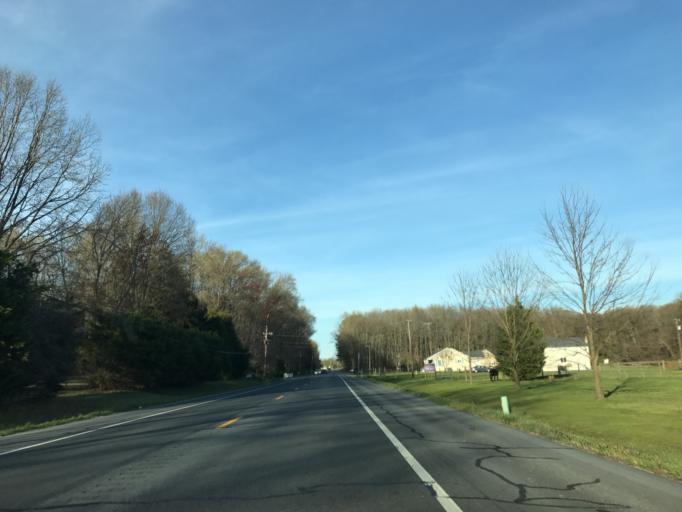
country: US
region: Delaware
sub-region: Kent County
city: Cheswold
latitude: 39.1417
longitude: -75.6834
